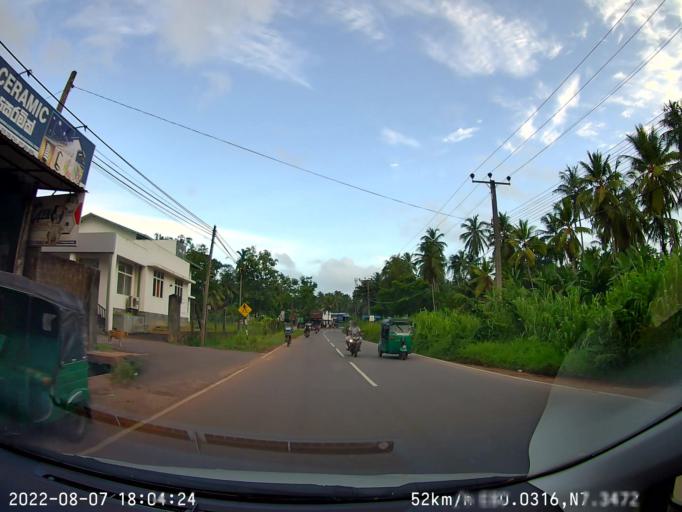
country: LK
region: North Western
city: Kuliyapitiya
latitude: 7.3471
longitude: 80.0316
